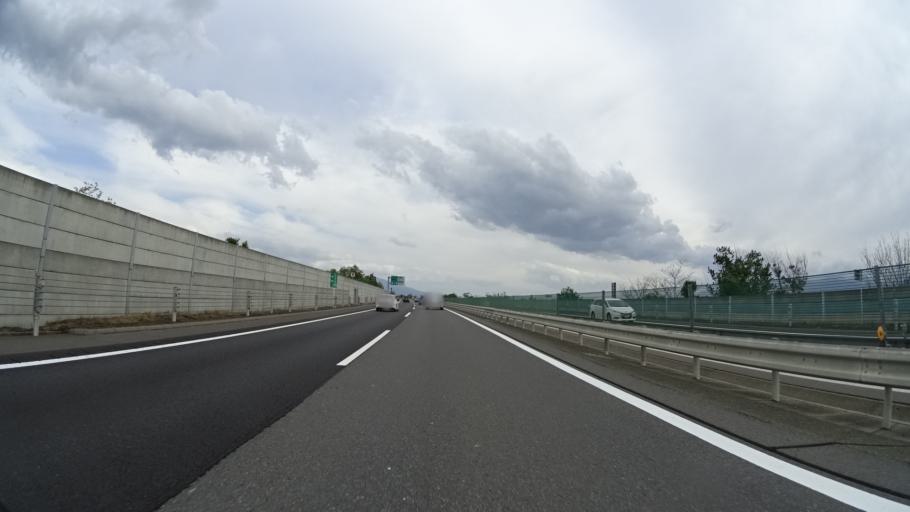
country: JP
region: Nagano
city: Toyoshina
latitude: 36.2872
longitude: 137.9287
